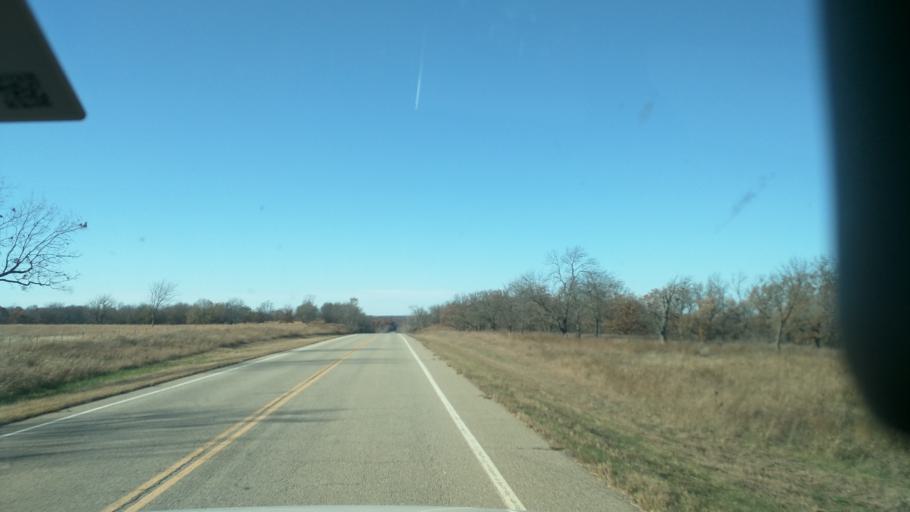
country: US
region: Oklahoma
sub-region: Nowata County
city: Nowata
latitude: 36.7432
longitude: -95.5241
